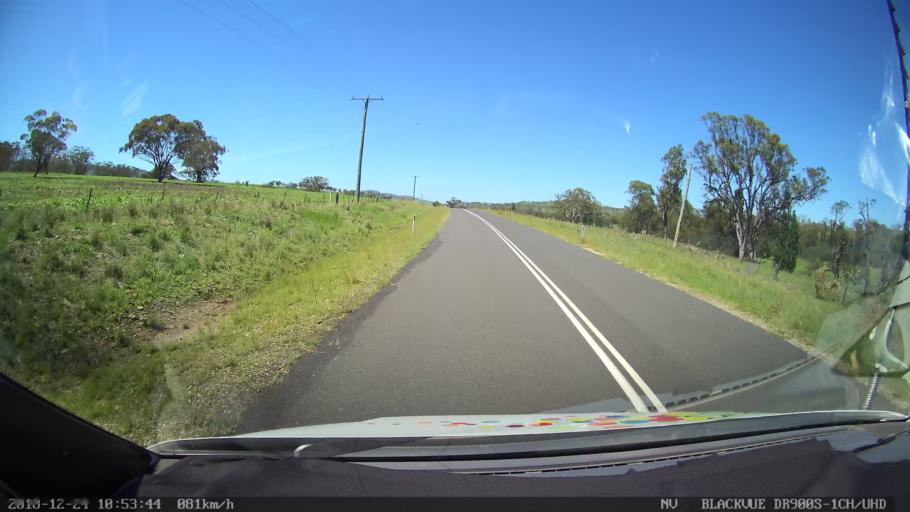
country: AU
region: New South Wales
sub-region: Upper Hunter Shire
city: Merriwa
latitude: -31.9949
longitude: 150.4192
